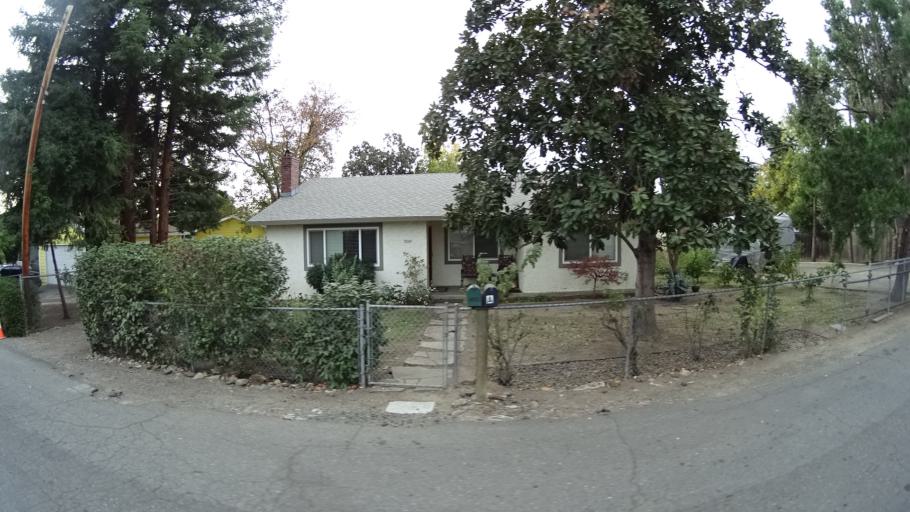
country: US
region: California
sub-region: Sacramento County
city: Citrus Heights
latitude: 38.7157
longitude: -121.2833
